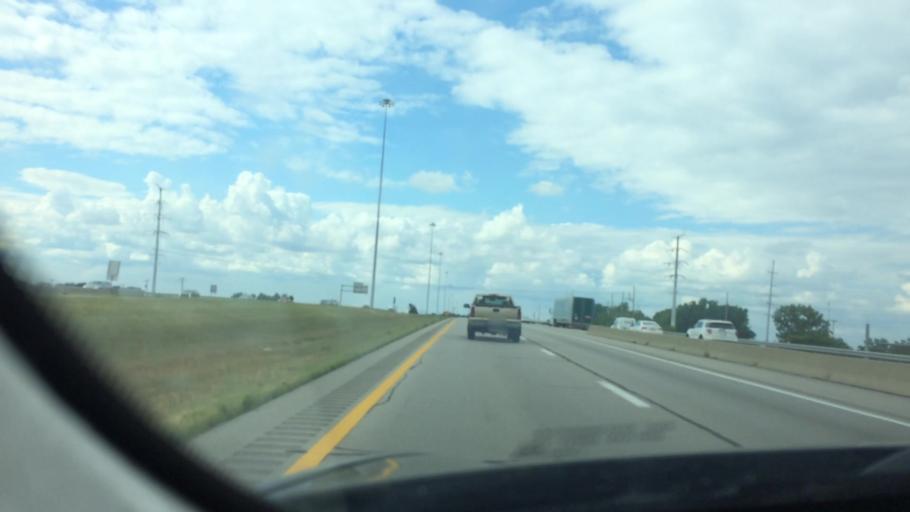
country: US
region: Ohio
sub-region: Lucas County
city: Maumee
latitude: 41.5566
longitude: -83.6869
